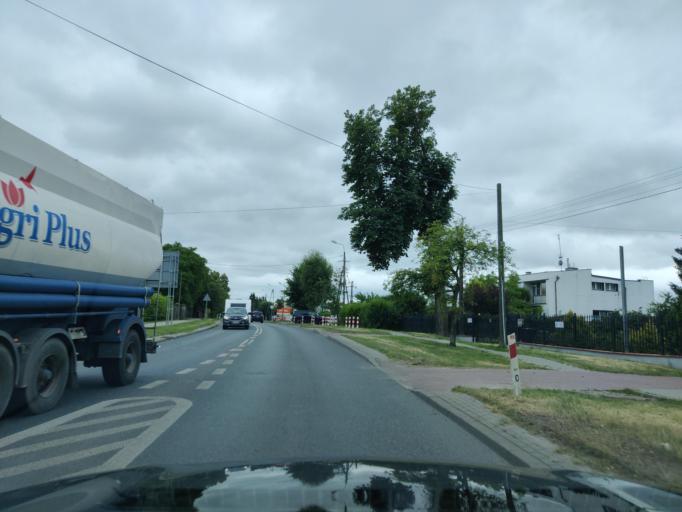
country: PL
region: Masovian Voivodeship
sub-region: Powiat pultuski
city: Pultusk
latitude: 52.6950
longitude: 21.0812
